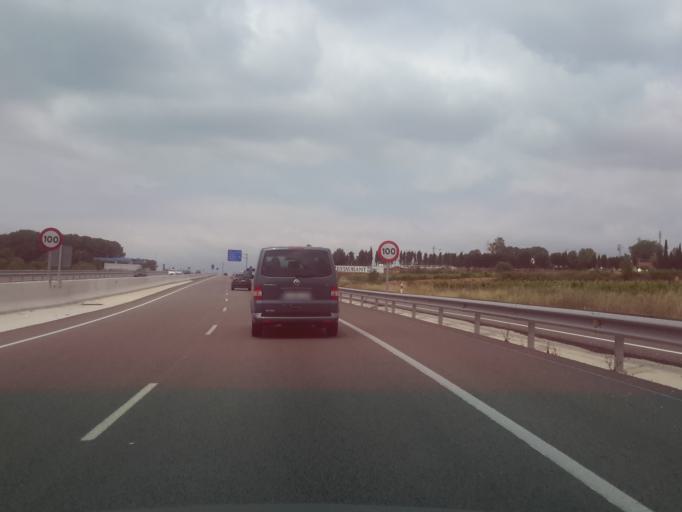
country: ES
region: Catalonia
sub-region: Provincia de Barcelona
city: Vilafranca del Penedes
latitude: 41.3227
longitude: 1.7235
